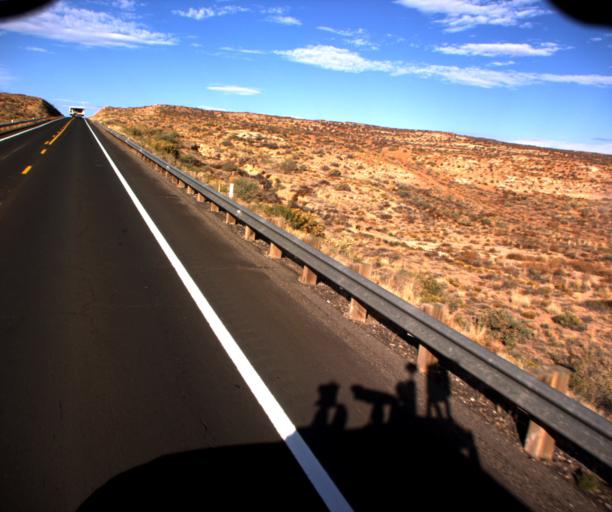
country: US
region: Arizona
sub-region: Apache County
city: Lukachukai
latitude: 36.9628
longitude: -109.4421
